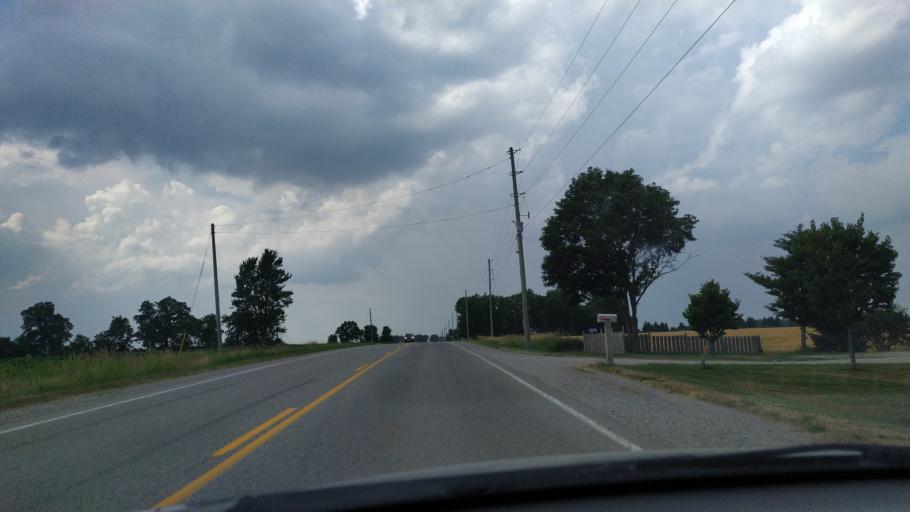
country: CA
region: Ontario
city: London
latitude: 43.1427
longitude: -81.1778
